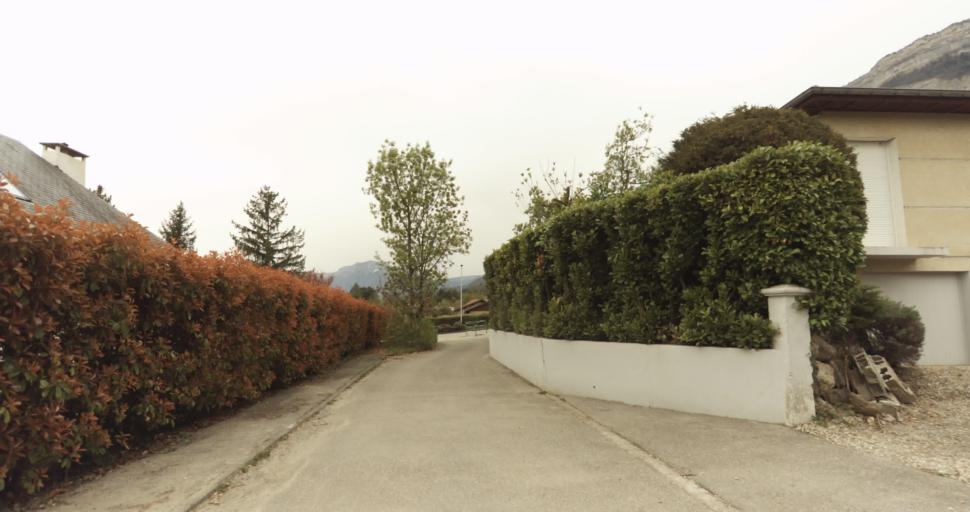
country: FR
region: Rhone-Alpes
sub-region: Departement de l'Isere
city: Biviers
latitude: 45.2284
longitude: 5.7958
